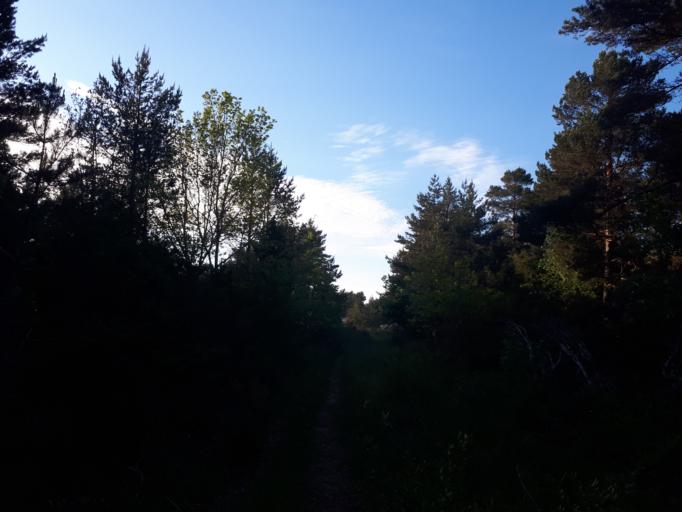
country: SE
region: Gotland
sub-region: Gotland
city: Visby
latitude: 57.6050
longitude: 18.2895
